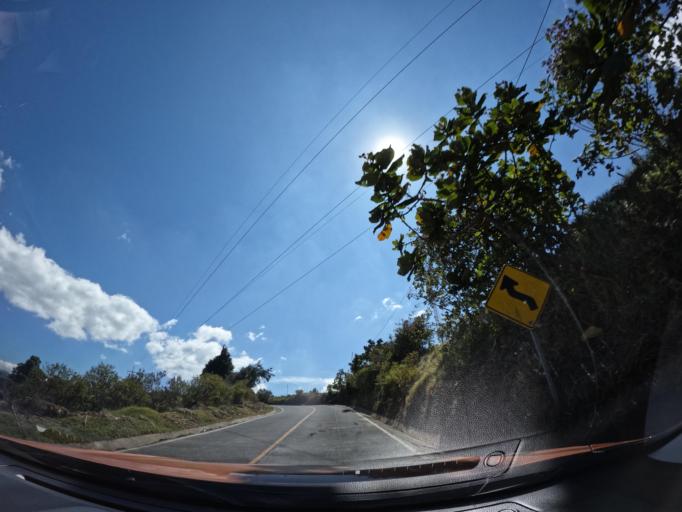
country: GT
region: Chimaltenango
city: Patzun
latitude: 14.6699
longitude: -91.0571
